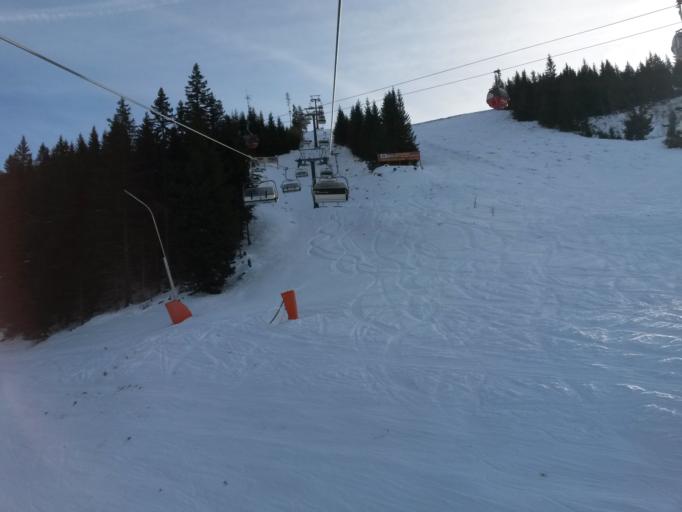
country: AT
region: Salzburg
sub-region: Politischer Bezirk Sankt Johann im Pongau
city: Dorfgastein
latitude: 47.2411
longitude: 13.1291
